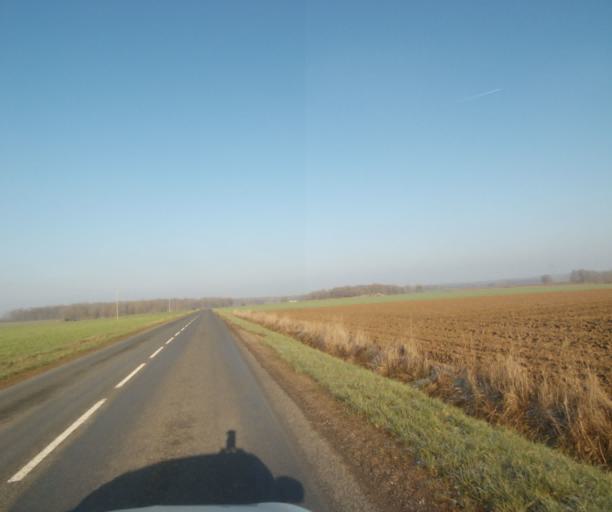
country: FR
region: Champagne-Ardenne
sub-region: Departement de la Haute-Marne
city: Montier-en-Der
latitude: 48.4982
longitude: 4.7524
